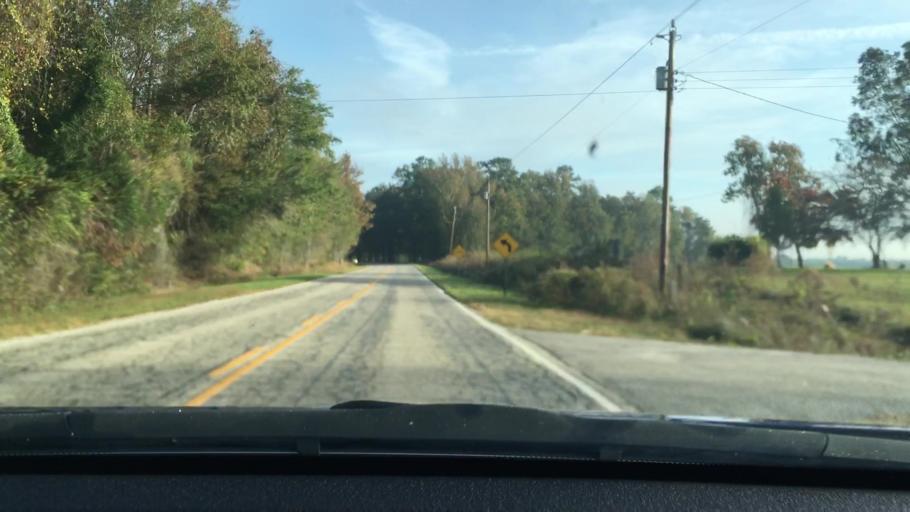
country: US
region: South Carolina
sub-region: Sumter County
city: East Sumter
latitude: 33.9951
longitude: -80.2905
